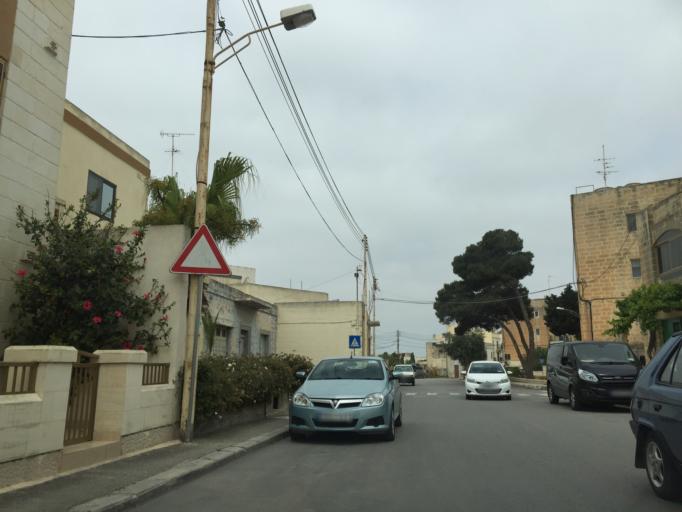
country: MT
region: Ir-Rabat
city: Rabat
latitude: 35.8828
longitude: 14.3911
